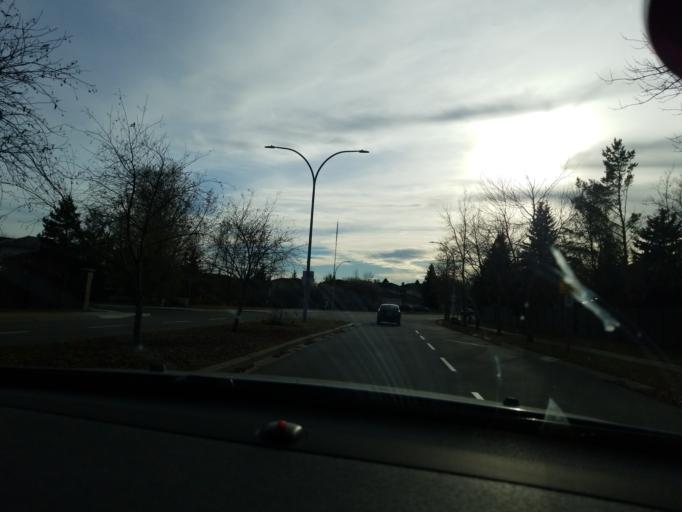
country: CA
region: Alberta
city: Sherwood Park
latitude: 53.5239
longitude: -113.2741
